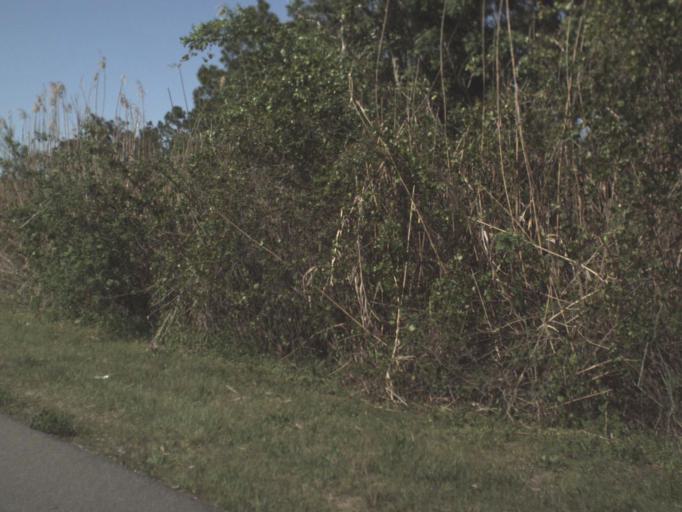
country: US
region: Florida
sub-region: Escambia County
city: East Pensacola Heights
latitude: 30.4768
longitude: -87.1632
